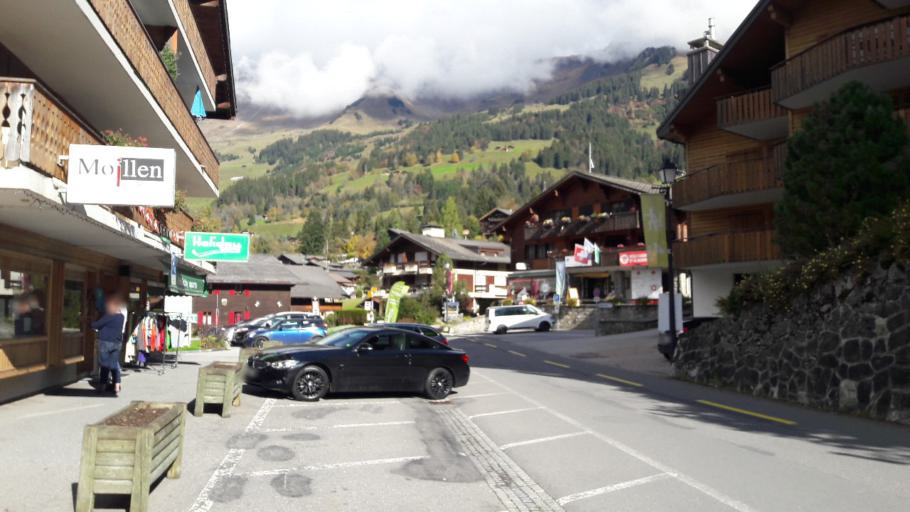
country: CH
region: Vaud
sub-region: Aigle District
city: Villars-sur-Ollon
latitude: 46.3494
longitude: 7.1573
